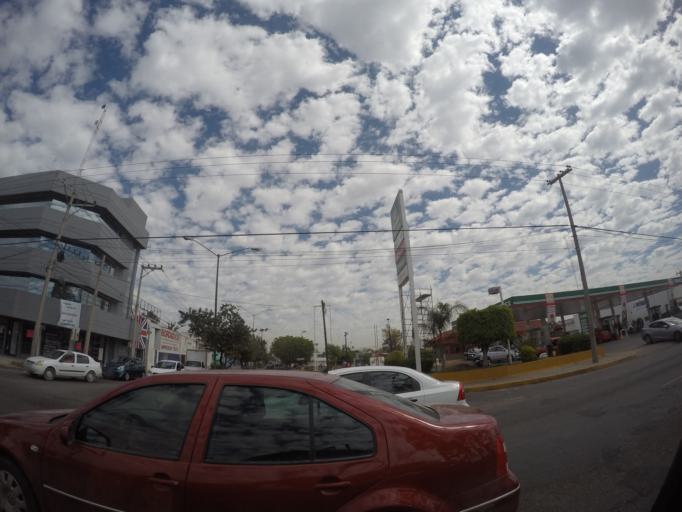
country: MX
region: Guanajuato
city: Leon
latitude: 21.1005
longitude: -101.6726
